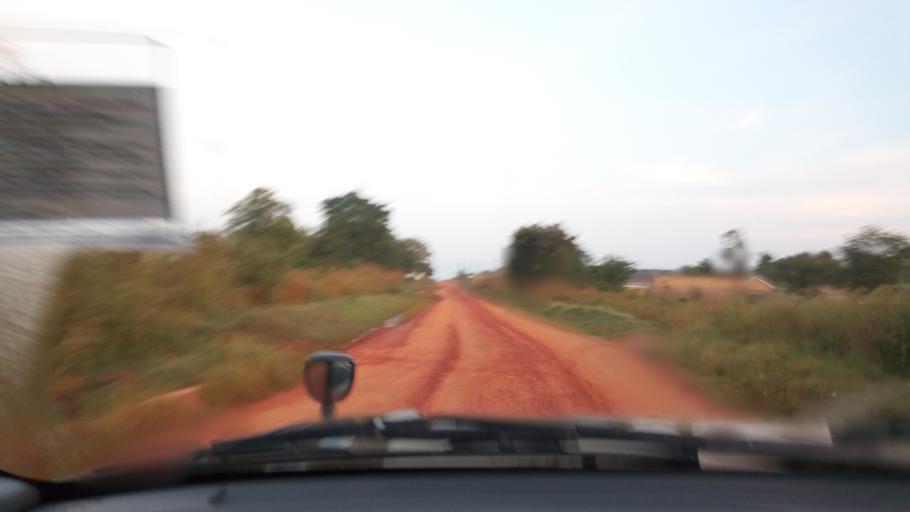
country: UG
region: Northern Region
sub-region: Adjumani District
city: Adjumani
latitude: 3.3897
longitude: 31.7908
